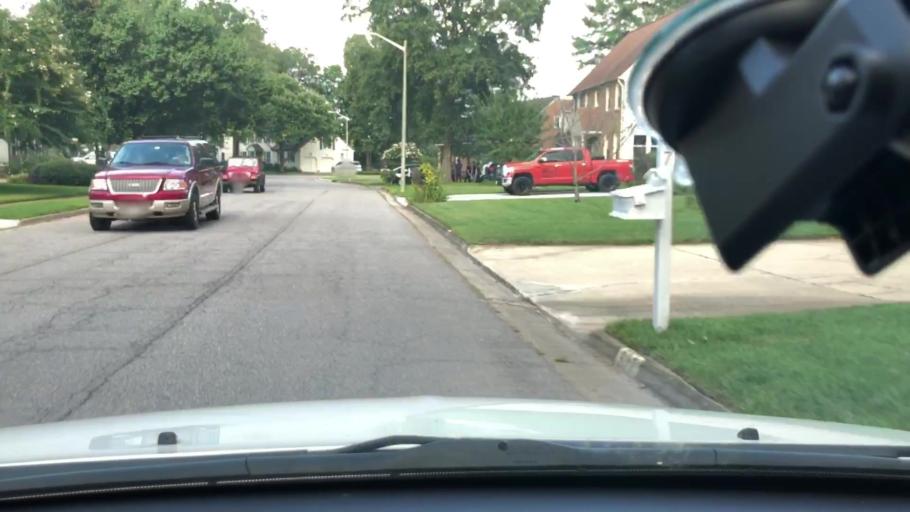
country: US
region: Virginia
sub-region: City of Chesapeake
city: Chesapeake
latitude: 36.7074
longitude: -76.2836
